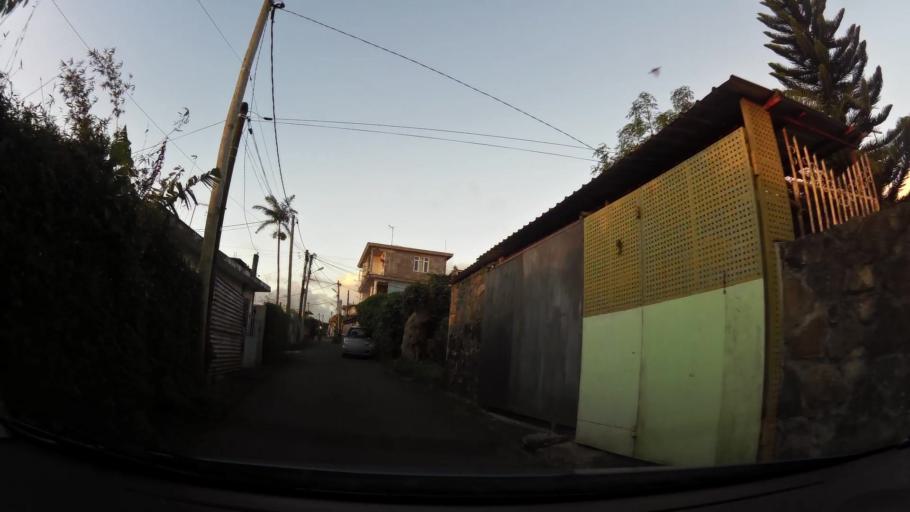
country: MU
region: Plaines Wilhems
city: Curepipe
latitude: -20.2986
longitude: 57.5235
